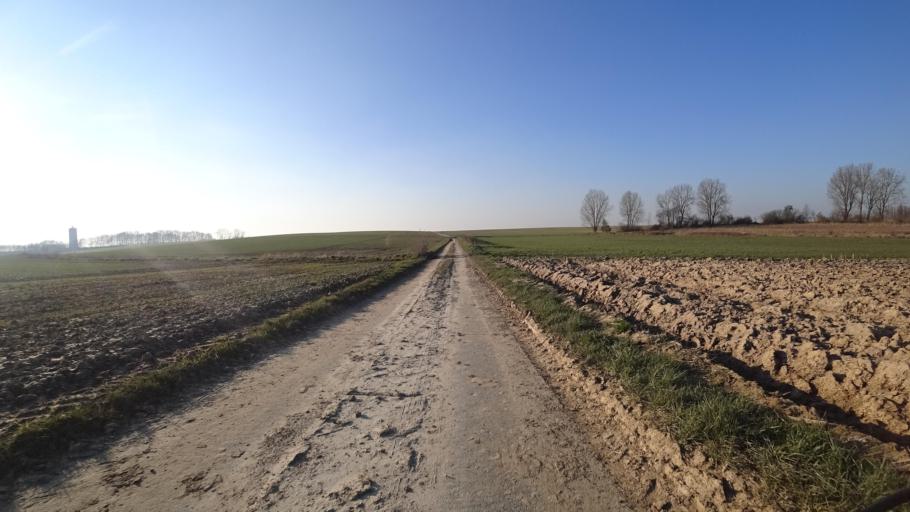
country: BE
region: Wallonia
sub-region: Province du Brabant Wallon
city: Chaumont-Gistoux
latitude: 50.6388
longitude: 4.7513
